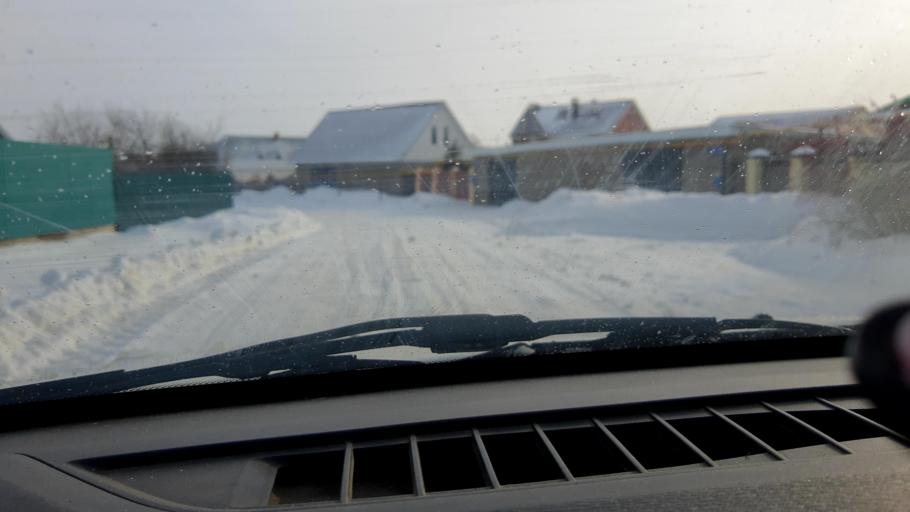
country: RU
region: Bashkortostan
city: Ufa
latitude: 54.5700
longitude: 55.9621
